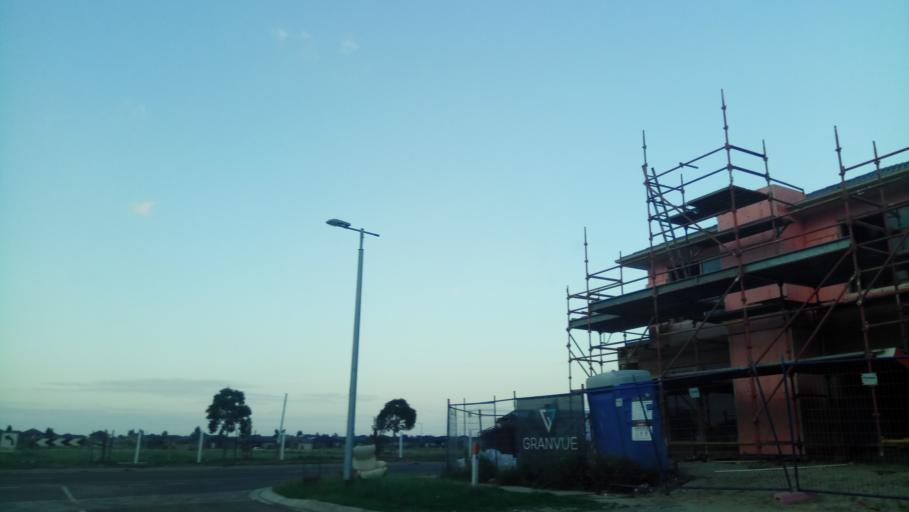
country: AU
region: Victoria
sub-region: Wyndham
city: Point Cook
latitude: -37.9119
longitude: 144.7665
